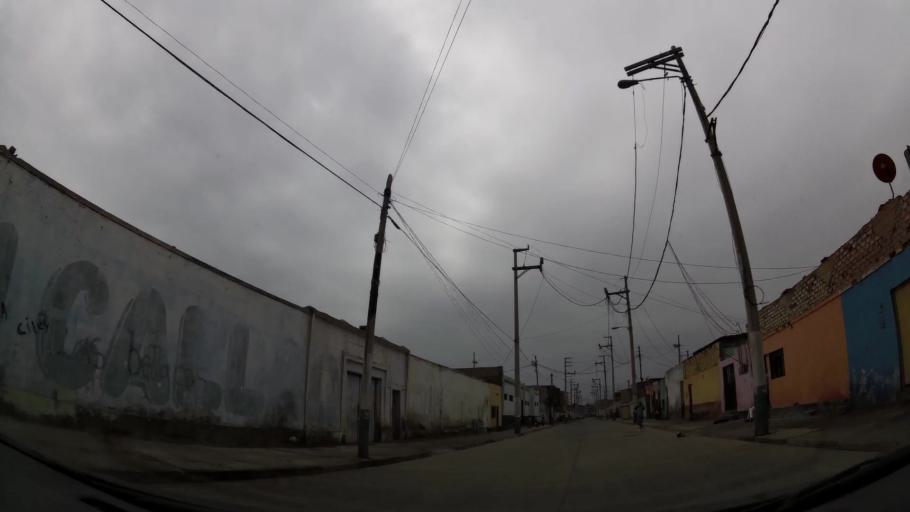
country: PE
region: Callao
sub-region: Callao
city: Callao
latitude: -12.0662
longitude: -77.1437
